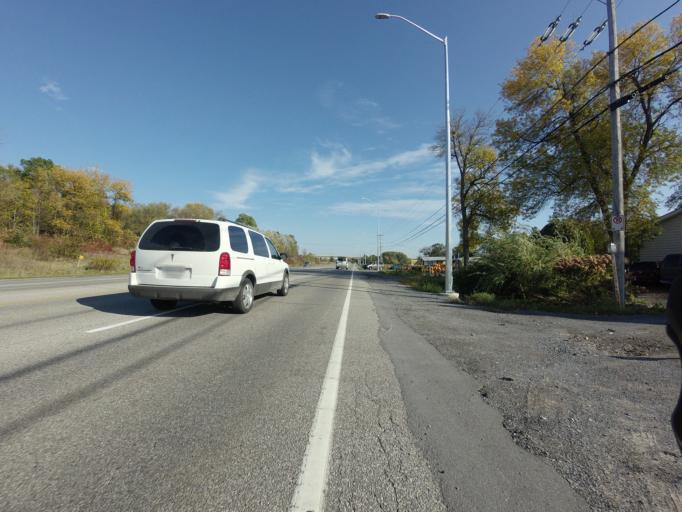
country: CA
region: Ontario
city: Kingston
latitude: 44.2403
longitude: -76.5982
